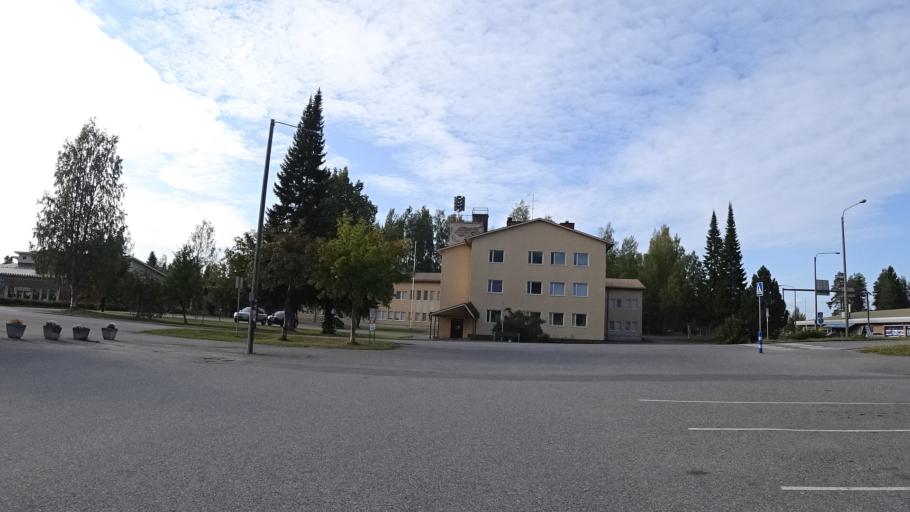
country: FI
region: North Karelia
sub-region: Joensuu
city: Eno
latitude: 62.7987
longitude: 30.1549
